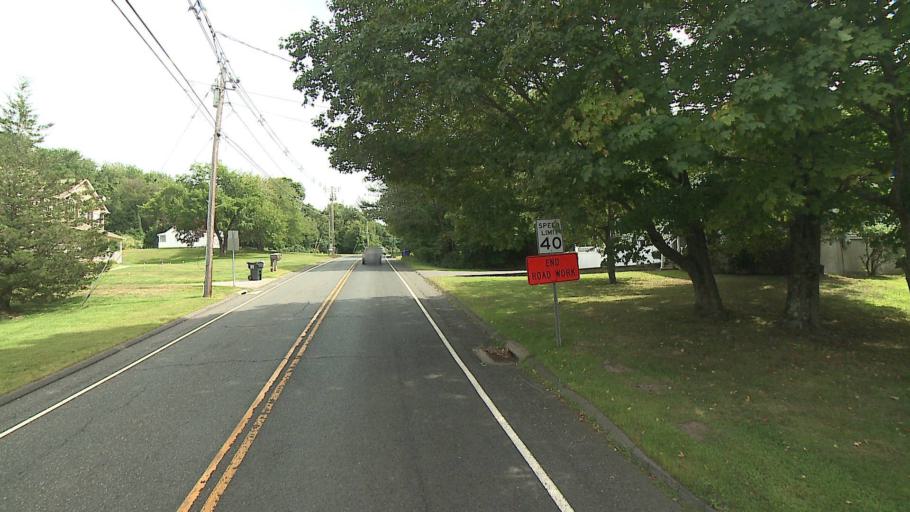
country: US
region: Connecticut
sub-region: Litchfield County
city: Watertown
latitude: 41.6214
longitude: -73.1069
